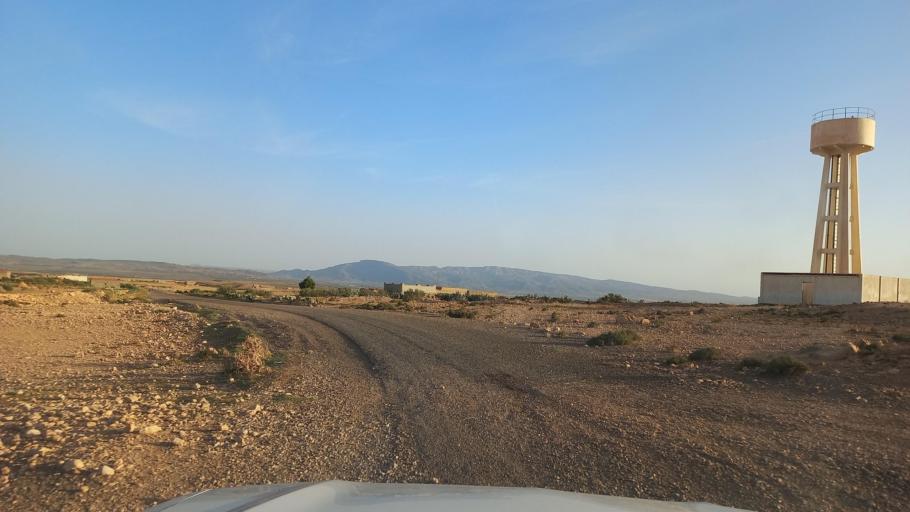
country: TN
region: Al Qasrayn
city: Kasserine
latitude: 35.2792
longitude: 8.9091
